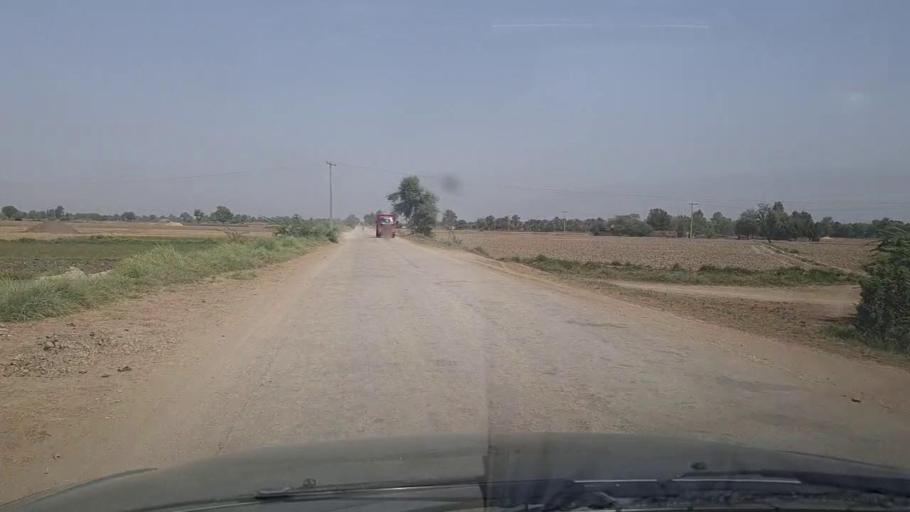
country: PK
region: Sindh
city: Setharja Old
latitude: 27.1350
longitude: 68.5302
